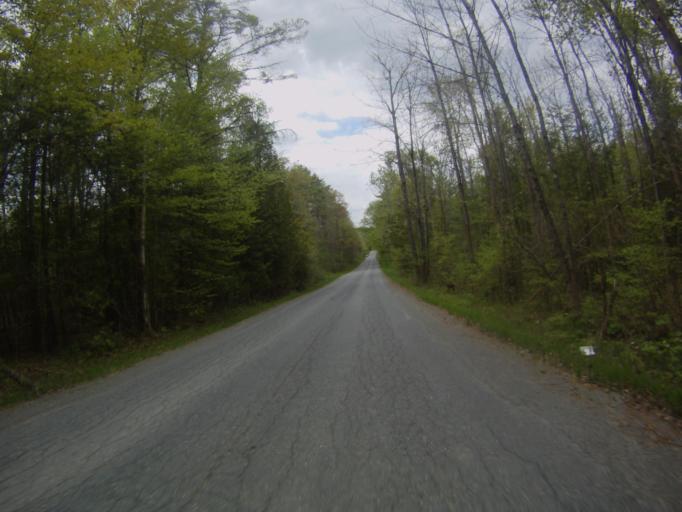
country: US
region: New York
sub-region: Essex County
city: Ticonderoga
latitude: 43.9276
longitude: -73.5052
